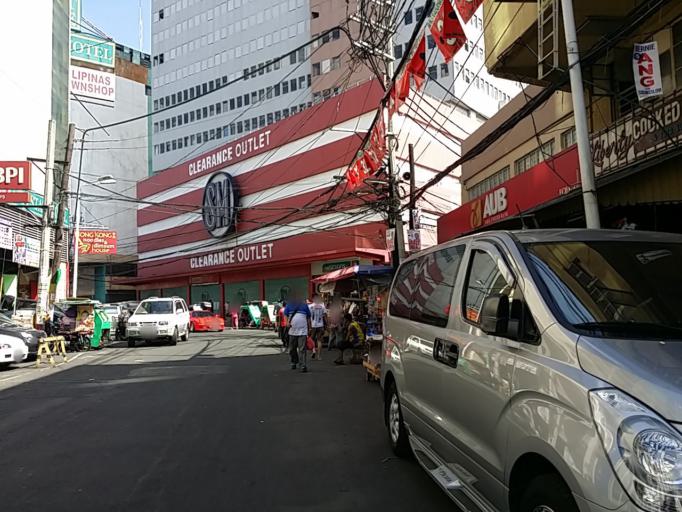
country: PH
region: Metro Manila
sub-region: City of Manila
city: Quiapo
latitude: 14.5979
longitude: 120.9822
